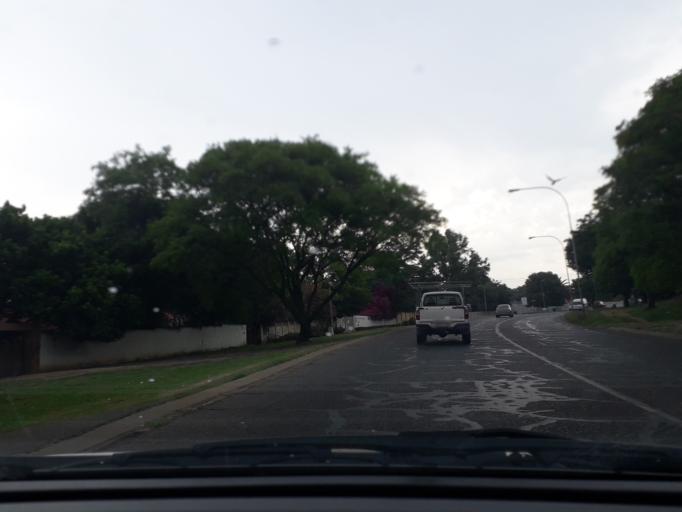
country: ZA
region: Gauteng
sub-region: City of Johannesburg Metropolitan Municipality
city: Johannesburg
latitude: -26.1471
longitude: 28.1031
